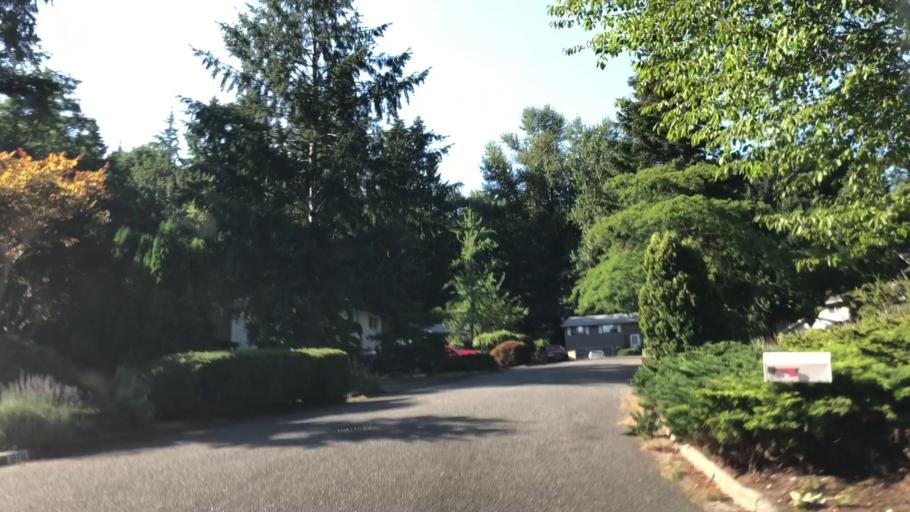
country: US
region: Washington
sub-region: Snohomish County
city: Brier
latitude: 47.7734
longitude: -122.2863
